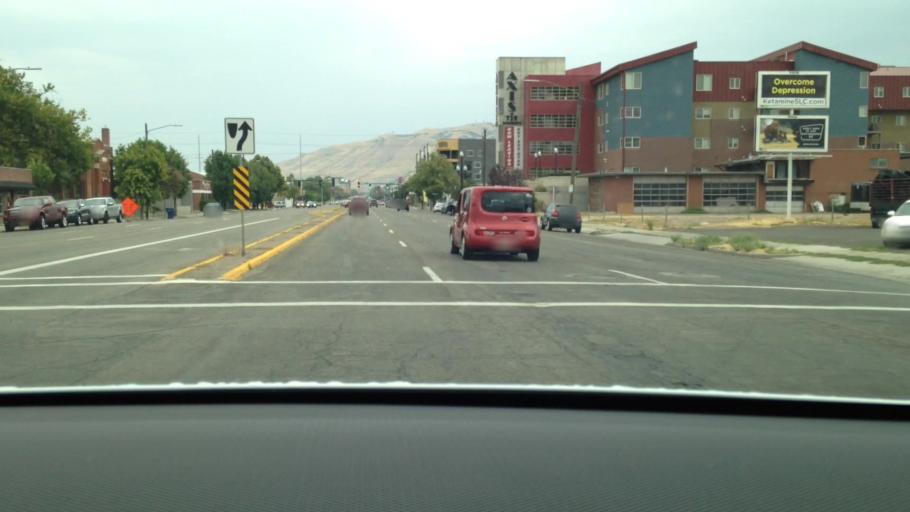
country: US
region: Utah
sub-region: Salt Lake County
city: Salt Lake City
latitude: 40.7520
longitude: -111.8997
